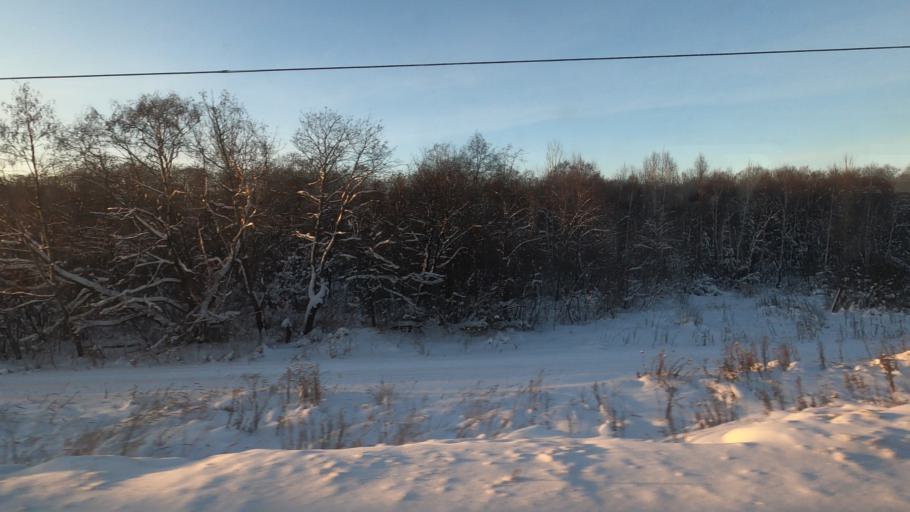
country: RU
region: Moskovskaya
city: Orud'yevo
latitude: 56.4415
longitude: 37.5132
